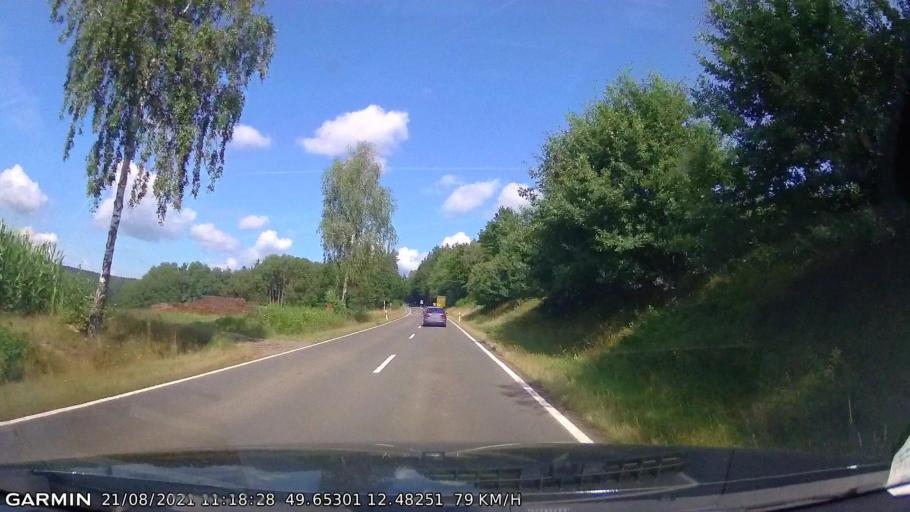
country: DE
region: Bavaria
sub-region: Upper Palatinate
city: Waidhaus
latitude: 49.6532
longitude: 12.4824
